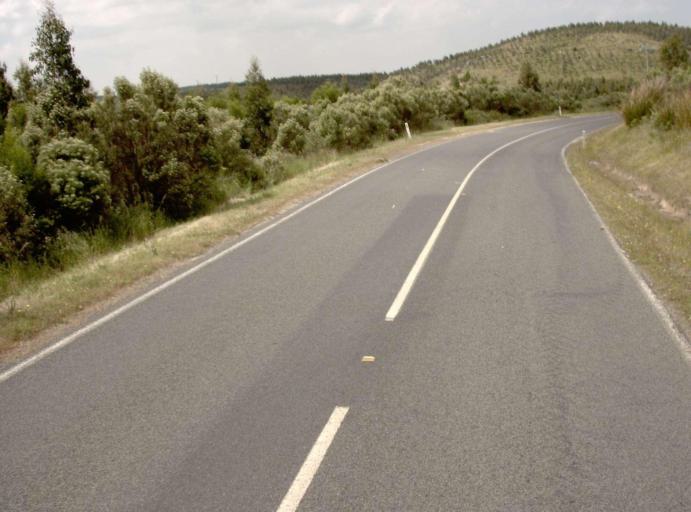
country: AU
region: Victoria
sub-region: Latrobe
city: Traralgon
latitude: -38.3824
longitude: 146.5674
